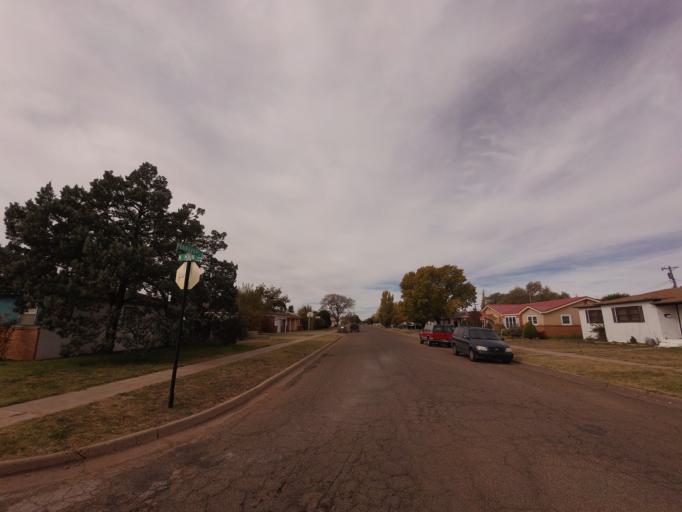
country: US
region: New Mexico
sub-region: Curry County
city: Clovis
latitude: 34.4246
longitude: -103.2071
